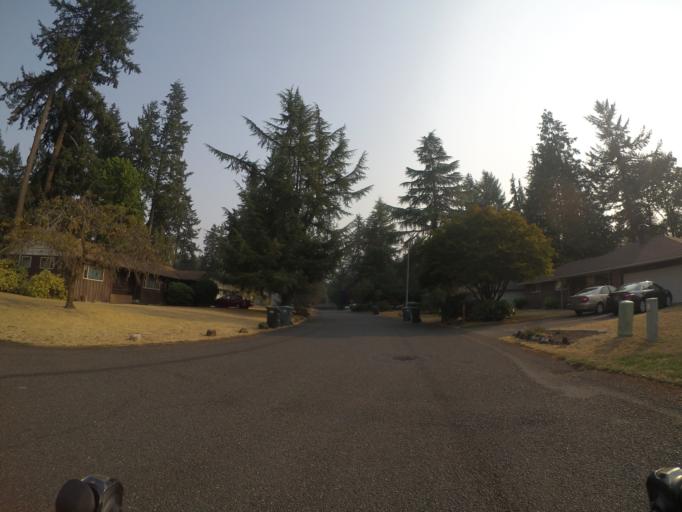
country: US
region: Washington
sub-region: Pierce County
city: Lakewood
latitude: 47.1505
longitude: -122.5199
